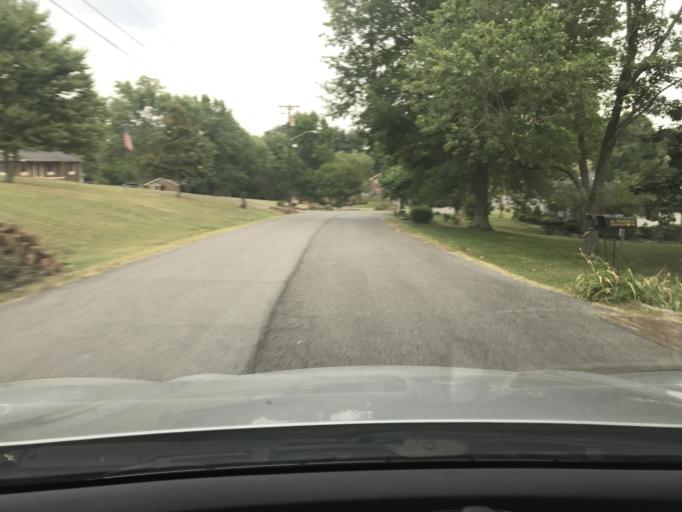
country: US
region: Tennessee
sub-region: Davidson County
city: Goodlettsville
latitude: 36.3040
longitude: -86.7121
